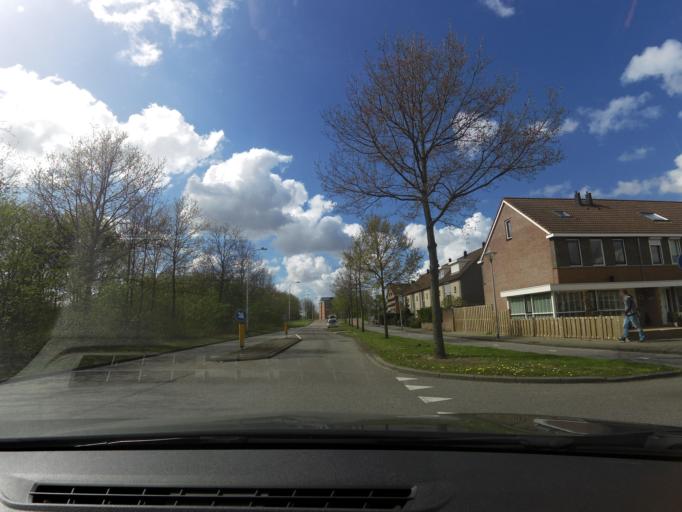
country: NL
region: South Holland
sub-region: Gemeente Albrandswaard
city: Rhoon
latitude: 51.8613
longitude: 4.3998
